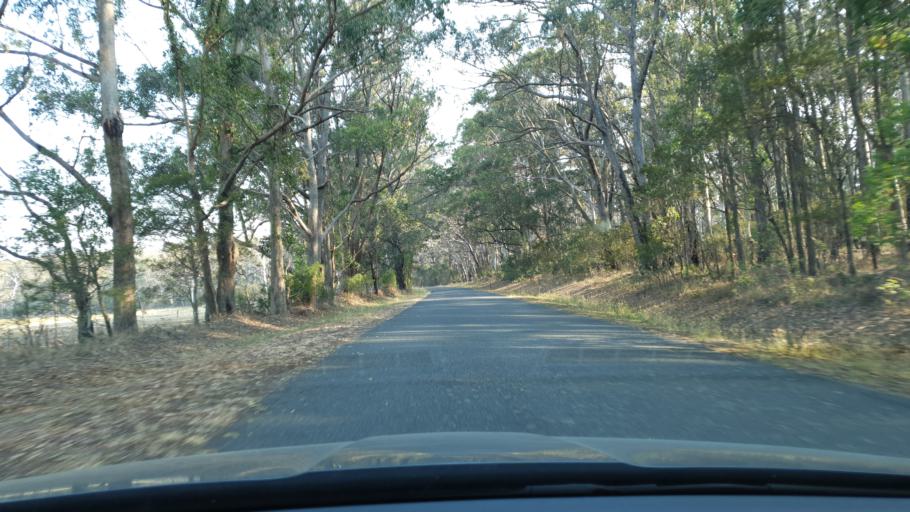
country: AU
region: New South Wales
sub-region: Tenterfield Municipality
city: Carrolls Creek
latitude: -28.6934
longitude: 152.0903
